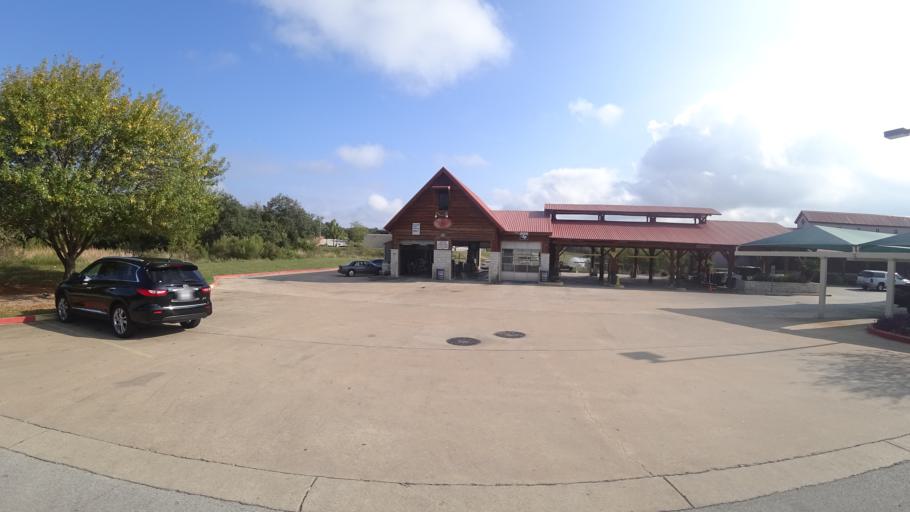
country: US
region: Texas
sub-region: Travis County
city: Bee Cave
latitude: 30.3063
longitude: -97.9333
